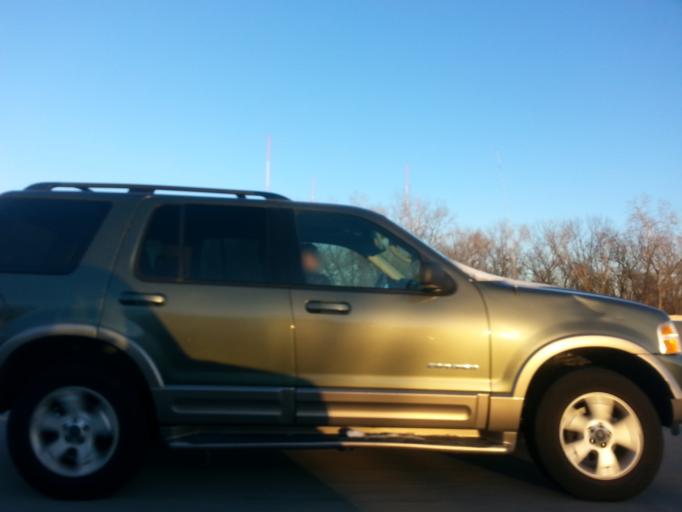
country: US
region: Illinois
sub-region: Cook County
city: Des Plaines
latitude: 42.0417
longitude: -87.8695
